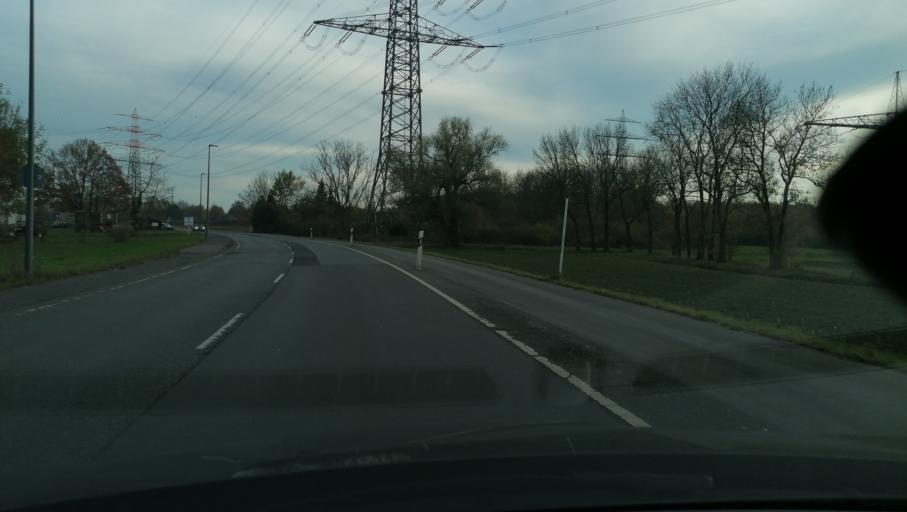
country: DE
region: North Rhine-Westphalia
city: Castrop-Rauxel
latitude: 51.5759
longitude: 7.3566
